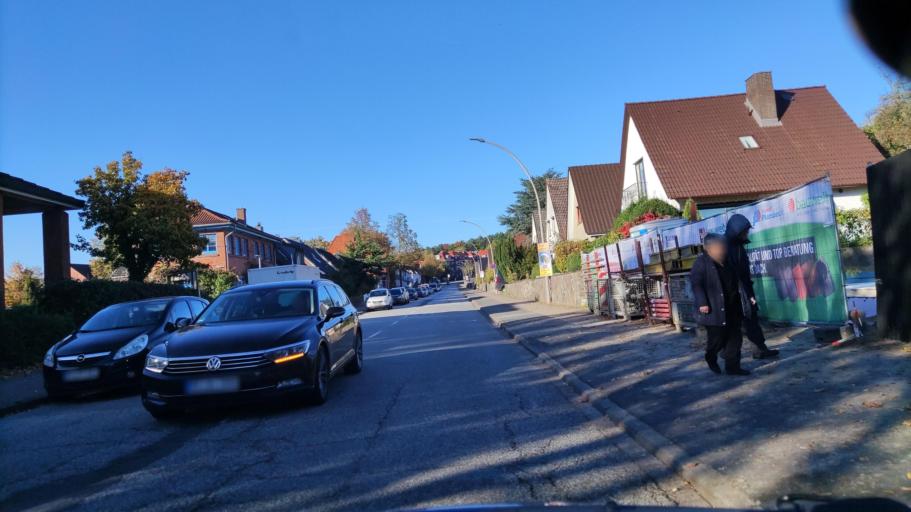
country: DE
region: Schleswig-Holstein
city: Geesthacht
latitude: 53.4396
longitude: 10.3725
